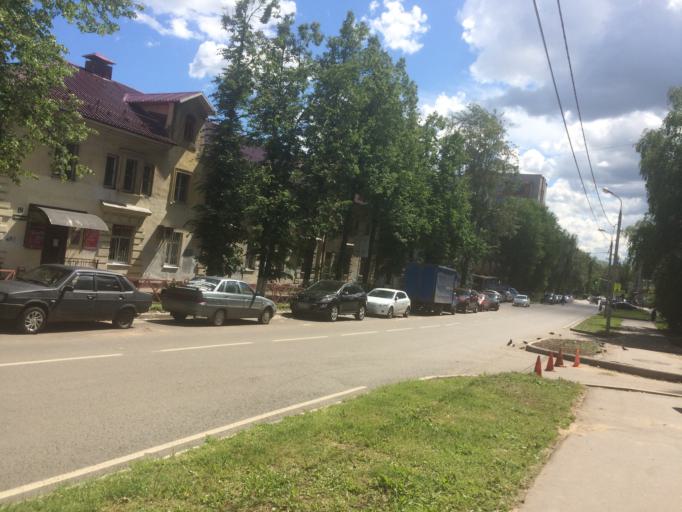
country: RU
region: Jaroslavl
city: Yaroslavl
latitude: 57.6229
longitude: 39.8623
